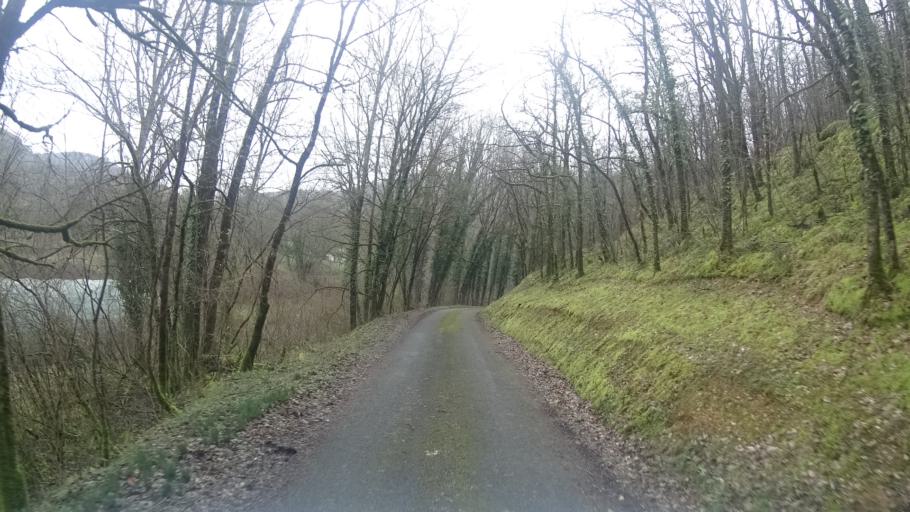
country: FR
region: Aquitaine
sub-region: Departement de la Dordogne
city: Terrasson-Lavilledieu
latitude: 45.1109
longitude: 1.2382
